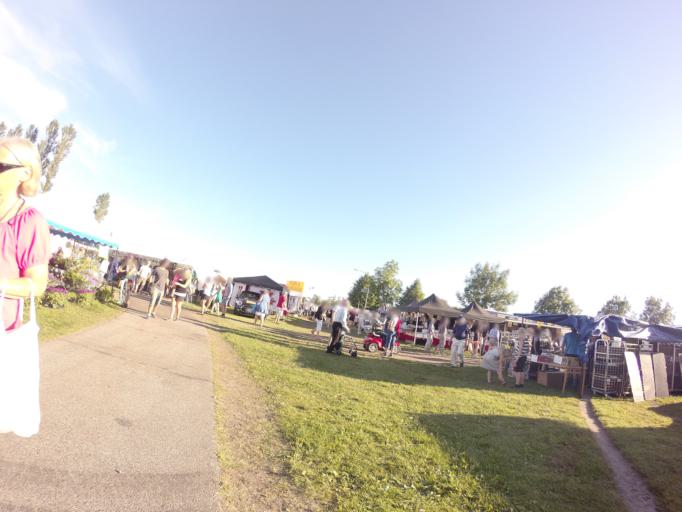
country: SE
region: Skane
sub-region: Sjobo Kommun
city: Sjoebo
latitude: 55.6313
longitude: 13.7110
